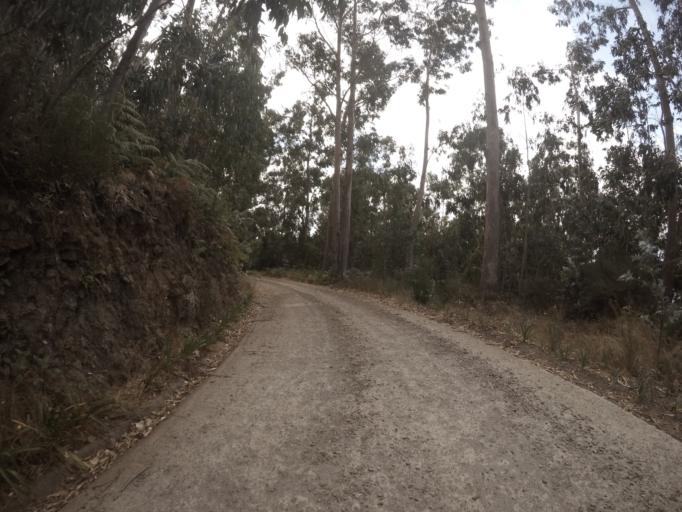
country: PT
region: Madeira
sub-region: Camara de Lobos
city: Curral das Freiras
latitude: 32.7091
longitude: -17.0102
